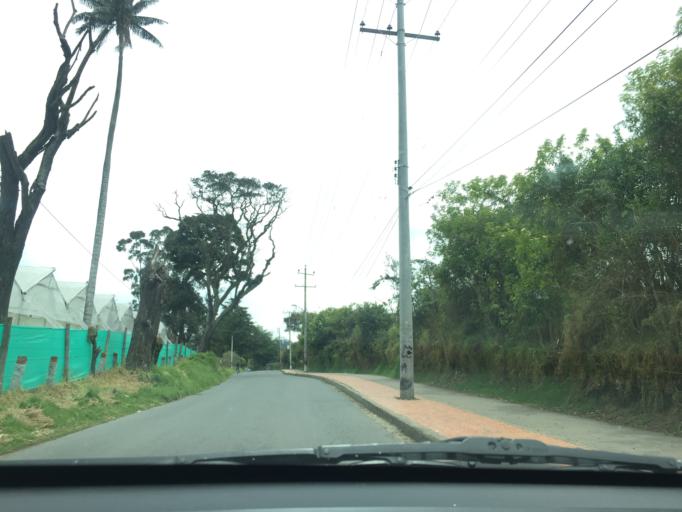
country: CO
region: Cundinamarca
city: El Rosal
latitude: 4.8462
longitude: -74.2584
